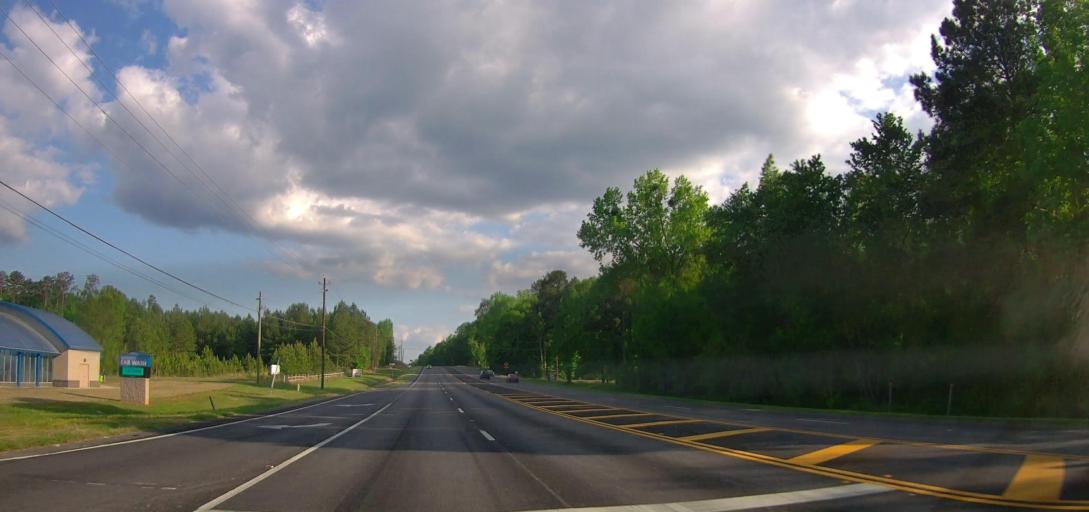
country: US
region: Georgia
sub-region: Baldwin County
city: Milledgeville
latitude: 33.1491
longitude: -83.2734
